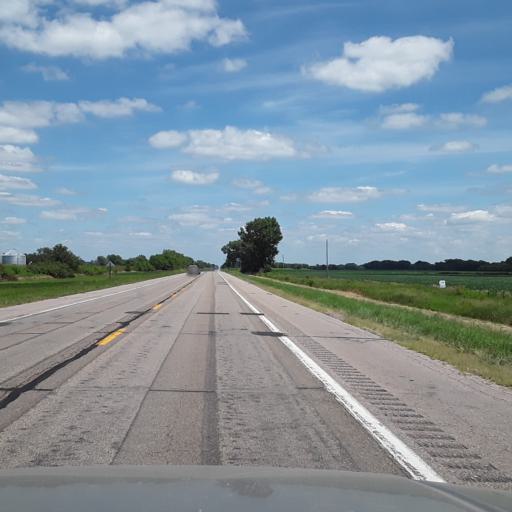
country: US
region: Nebraska
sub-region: Polk County
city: Osceola
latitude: 41.3539
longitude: -97.5744
